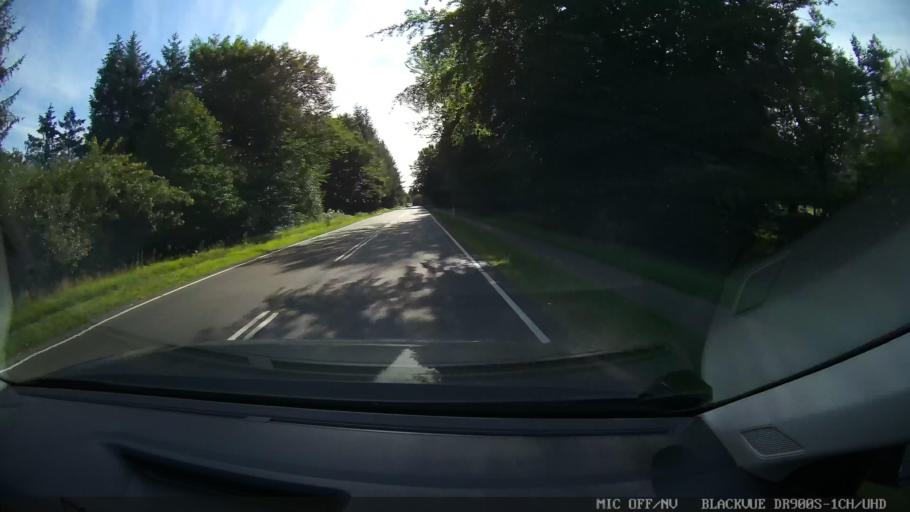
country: DK
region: North Denmark
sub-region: Mariagerfjord Kommune
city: Arden
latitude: 56.7806
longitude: 9.7562
